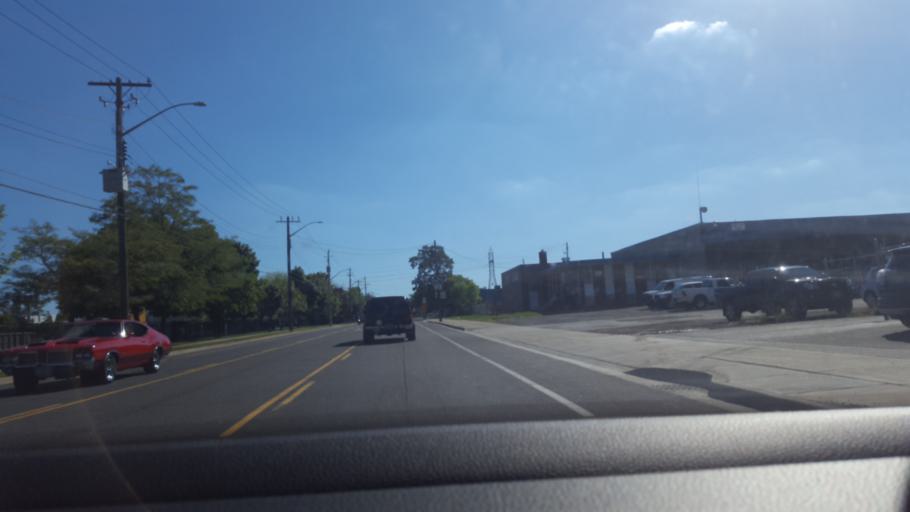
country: CA
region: Ontario
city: Hamilton
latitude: 43.2525
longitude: -79.7747
